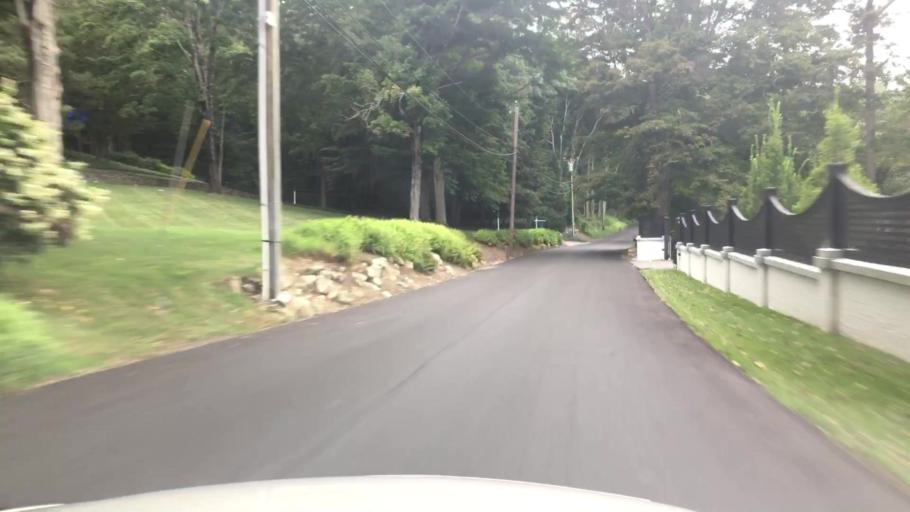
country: US
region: Connecticut
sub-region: Middlesex County
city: Essex Village
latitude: 41.3825
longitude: -72.3936
